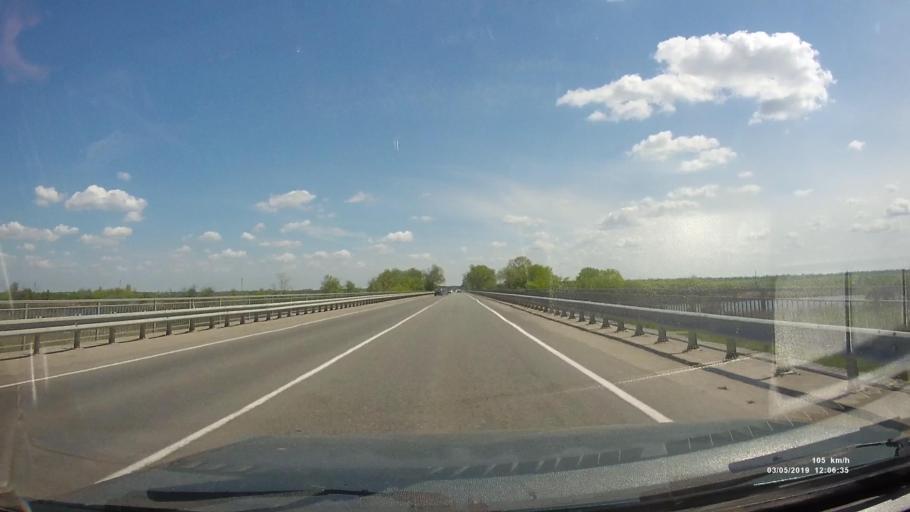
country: RU
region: Rostov
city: Bagayevskaya
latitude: 47.2851
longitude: 40.4550
